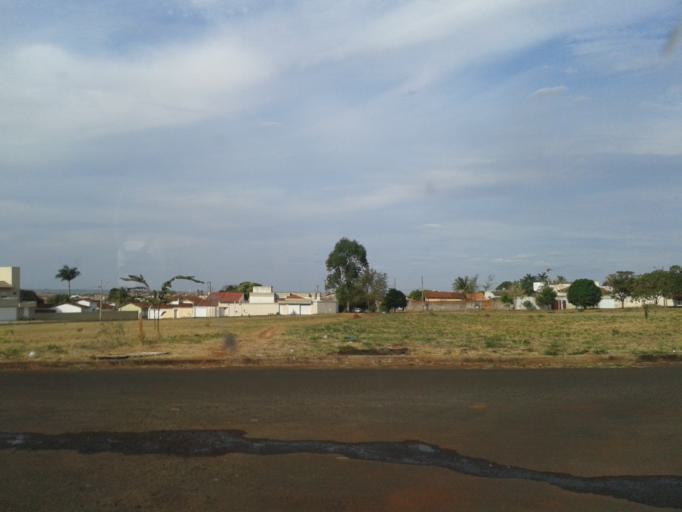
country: BR
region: Minas Gerais
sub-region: Ituiutaba
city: Ituiutaba
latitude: -18.9910
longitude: -49.4537
